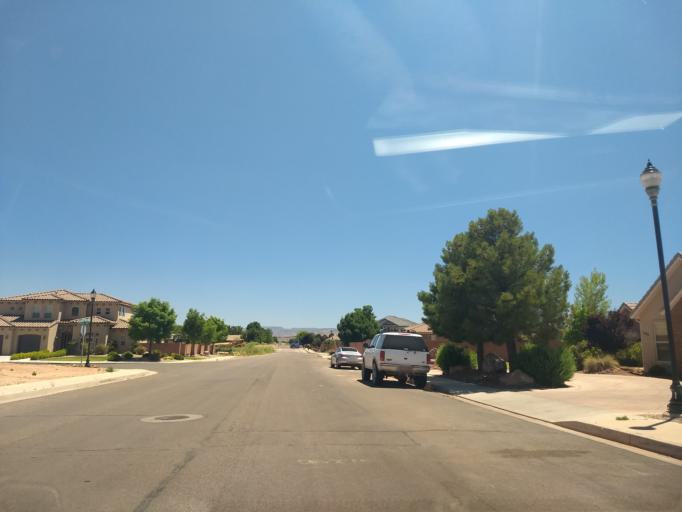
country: US
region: Utah
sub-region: Washington County
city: Washington
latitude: 37.1024
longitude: -113.5136
